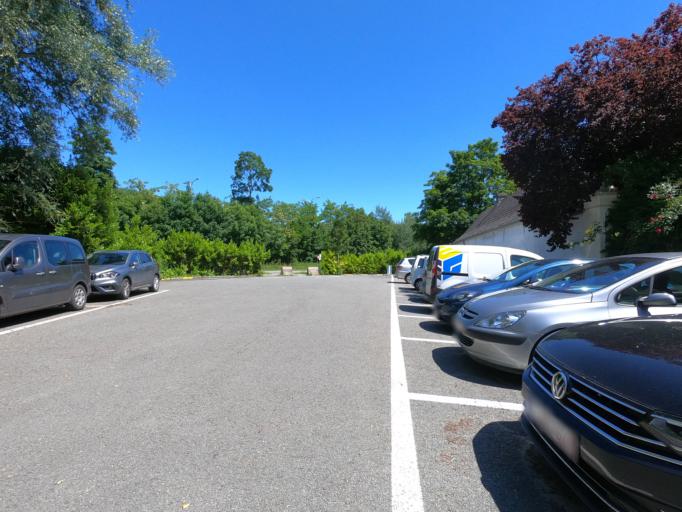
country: BE
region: Flanders
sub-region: Provincie Oost-Vlaanderen
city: Gent
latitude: 51.0523
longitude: 3.6695
